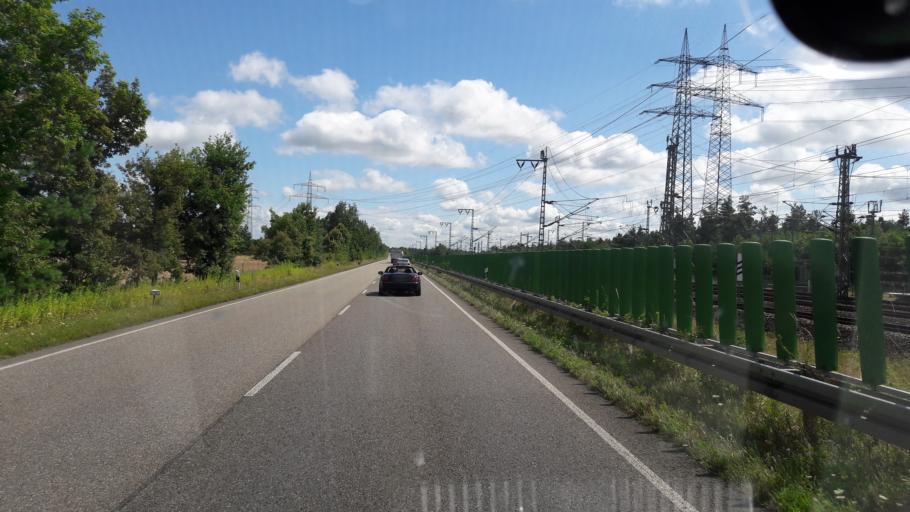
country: DE
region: Baden-Wuerttemberg
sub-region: Karlsruhe Region
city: Waghausel
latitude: 49.2227
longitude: 8.4977
